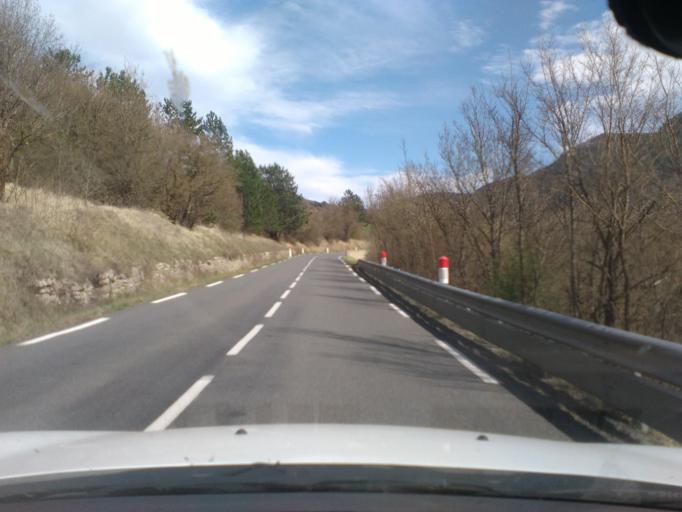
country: FR
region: Languedoc-Roussillon
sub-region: Departement de la Lozere
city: Mende
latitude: 44.4592
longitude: 3.5226
